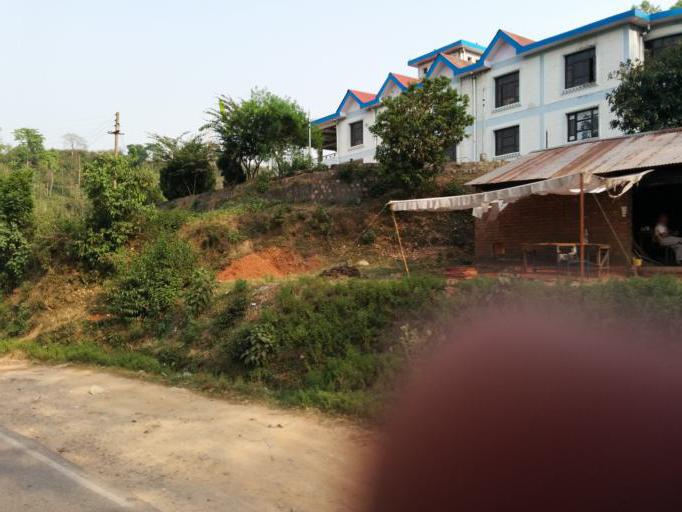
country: IN
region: Himachal Pradesh
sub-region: Kangra
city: Kotla
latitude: 32.2985
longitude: 75.9047
